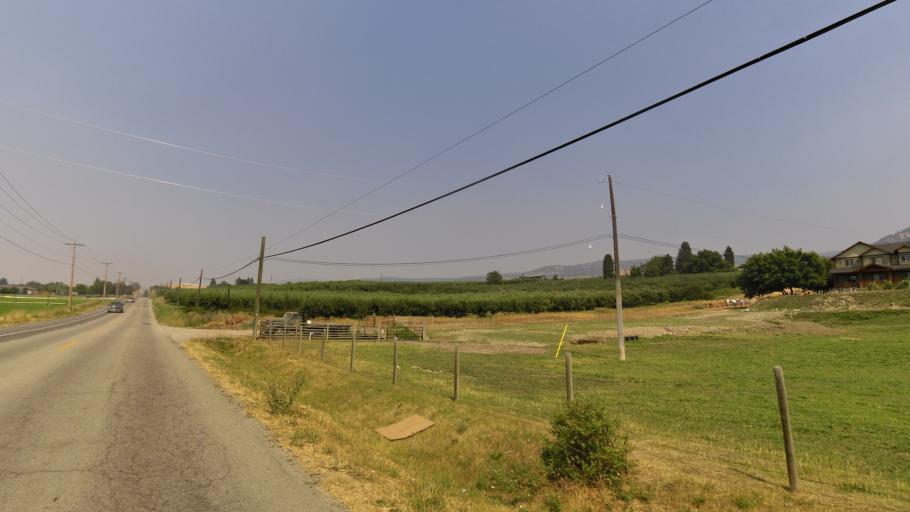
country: CA
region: British Columbia
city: Kelowna
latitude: 49.9234
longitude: -119.3641
